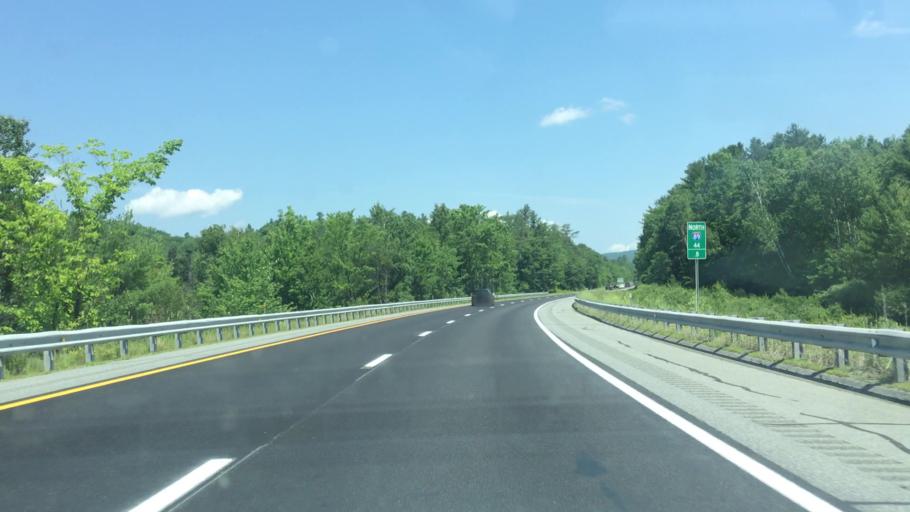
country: US
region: New Hampshire
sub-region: Sullivan County
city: Grantham
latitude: 43.5232
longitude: -72.1414
